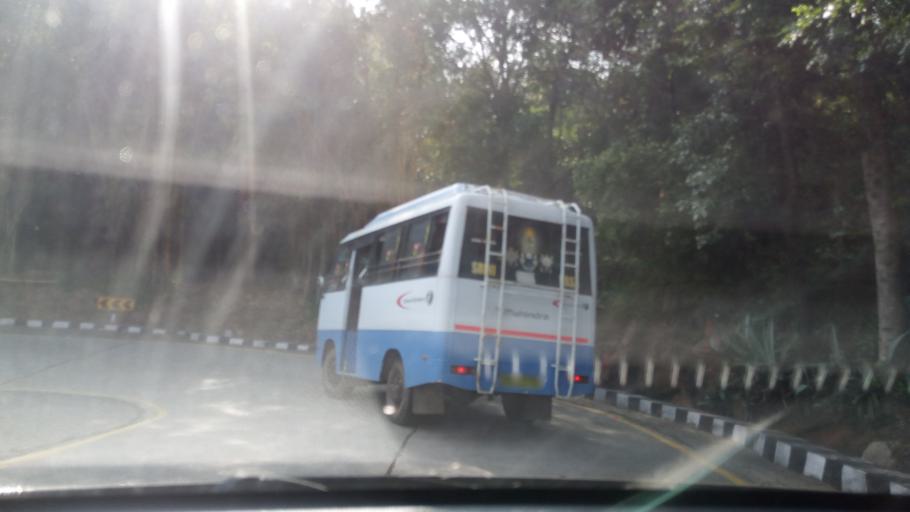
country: IN
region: Andhra Pradesh
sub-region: Chittoor
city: Tirumala
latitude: 13.6693
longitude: 79.3549
